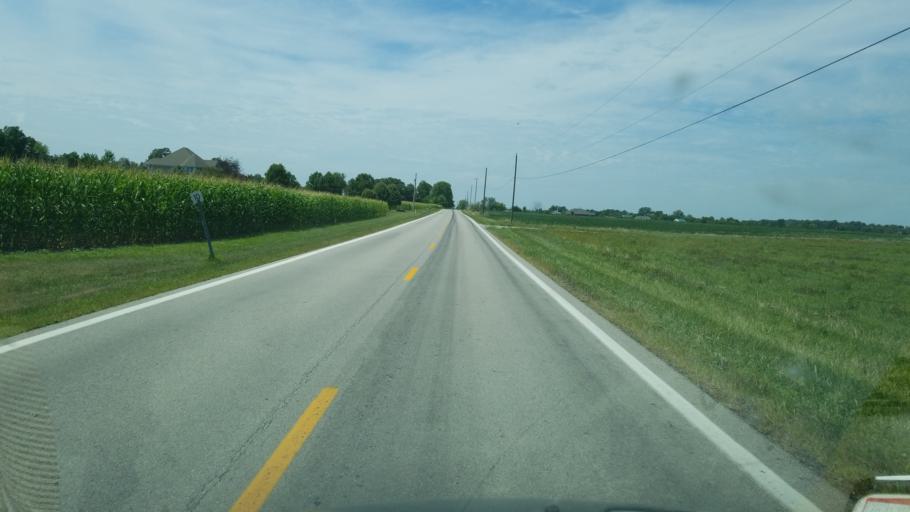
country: US
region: Ohio
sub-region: Madison County
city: West Jefferson
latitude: 39.8654
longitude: -83.2677
